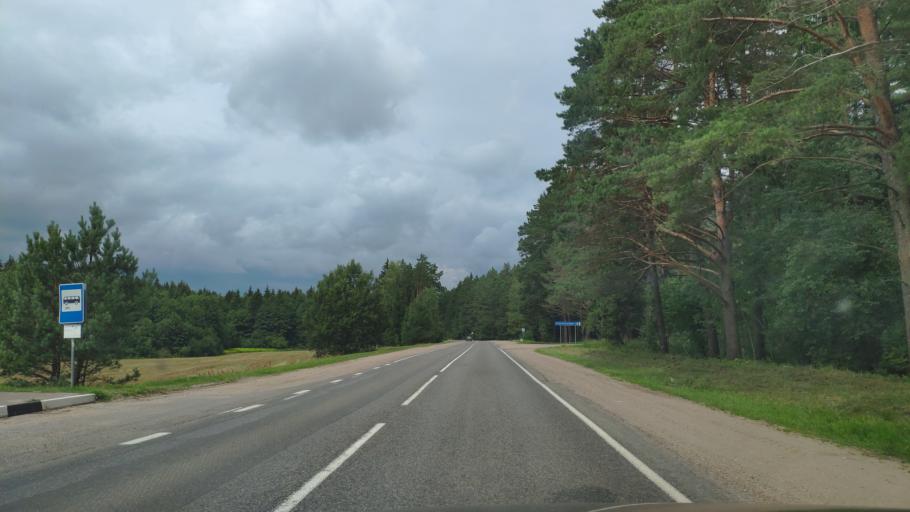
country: BY
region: Minsk
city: Zaslawye
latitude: 53.9700
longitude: 27.2471
